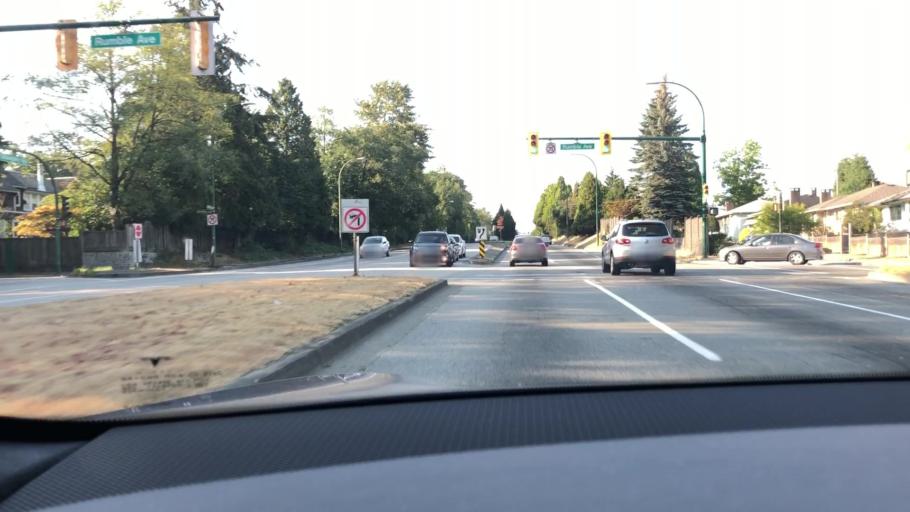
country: CA
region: British Columbia
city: Burnaby
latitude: 49.2146
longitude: -123.0237
